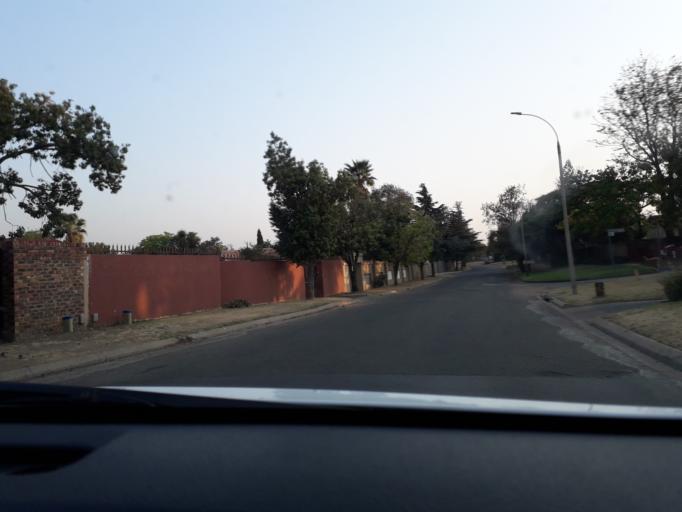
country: ZA
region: Gauteng
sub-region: City of Johannesburg Metropolitan Municipality
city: Modderfontein
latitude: -26.0683
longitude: 28.2007
